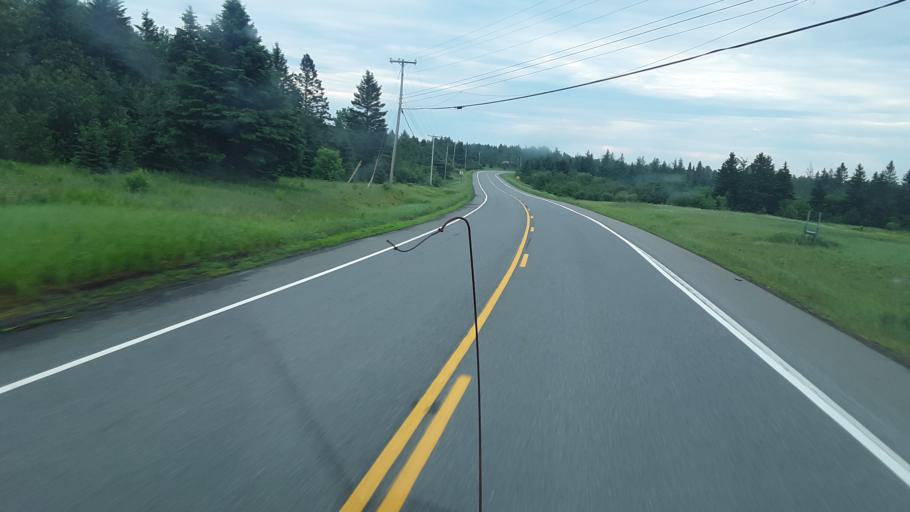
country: US
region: Maine
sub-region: Aroostook County
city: Presque Isle
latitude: 46.5922
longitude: -68.3864
